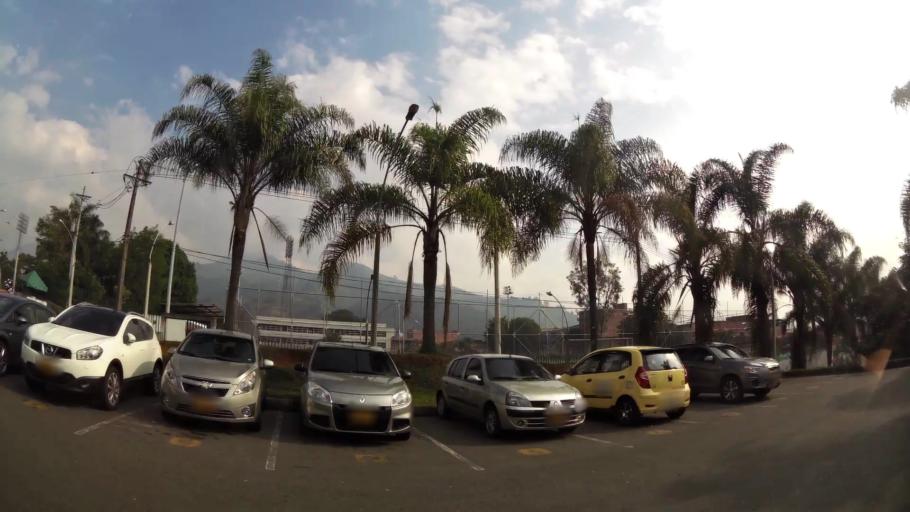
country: CO
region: Antioquia
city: Sabaneta
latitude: 6.1668
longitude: -75.6262
